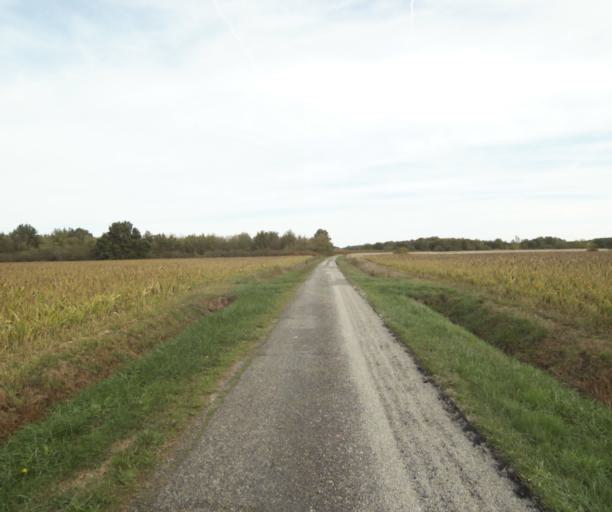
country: FR
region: Midi-Pyrenees
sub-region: Departement du Tarn-et-Garonne
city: Orgueil
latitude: 43.8812
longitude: 1.3893
